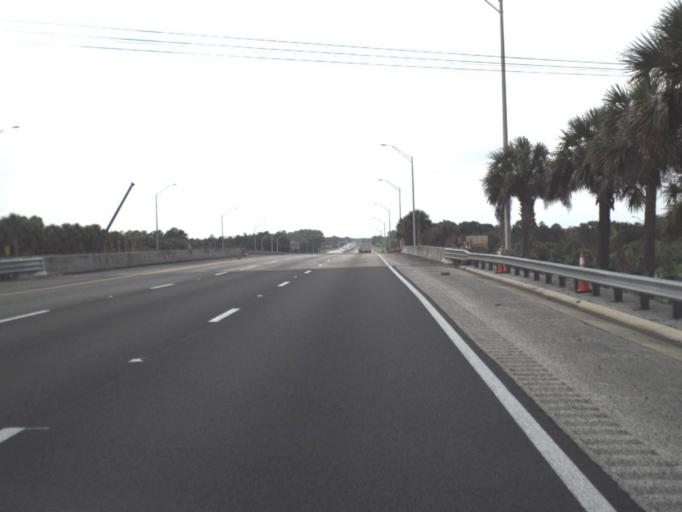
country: US
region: Florida
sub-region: Flagler County
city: Palm Coast
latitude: 29.6622
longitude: -81.2868
